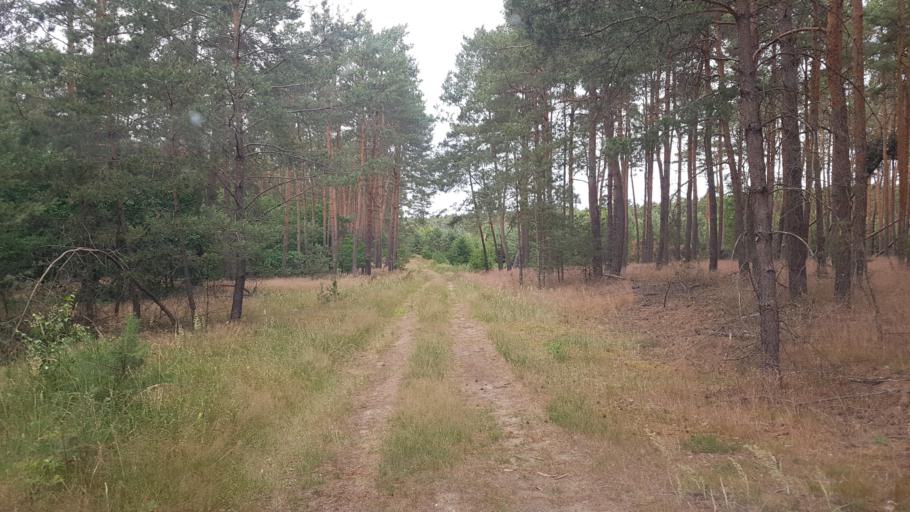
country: DE
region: Brandenburg
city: Treuenbrietzen
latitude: 52.0452
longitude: 12.8212
